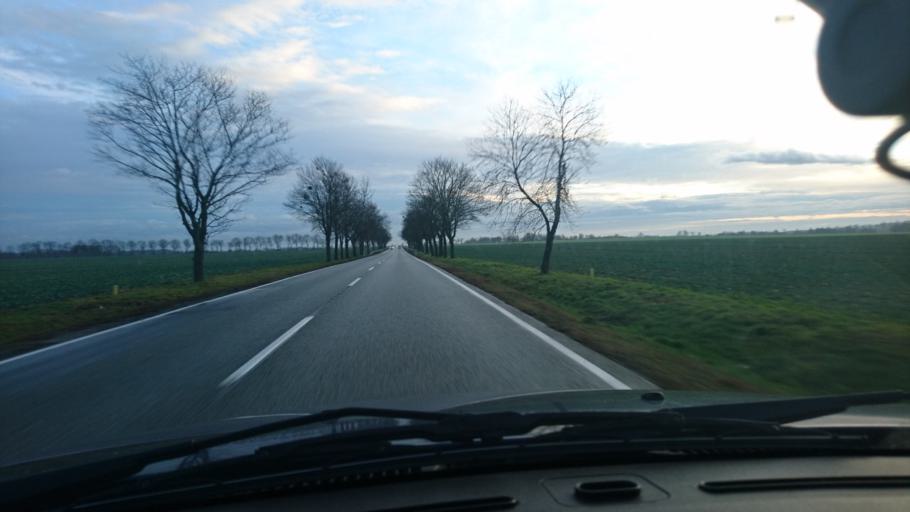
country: PL
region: Opole Voivodeship
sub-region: Powiat kluczborski
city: Byczyna
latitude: 51.0760
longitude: 18.2013
